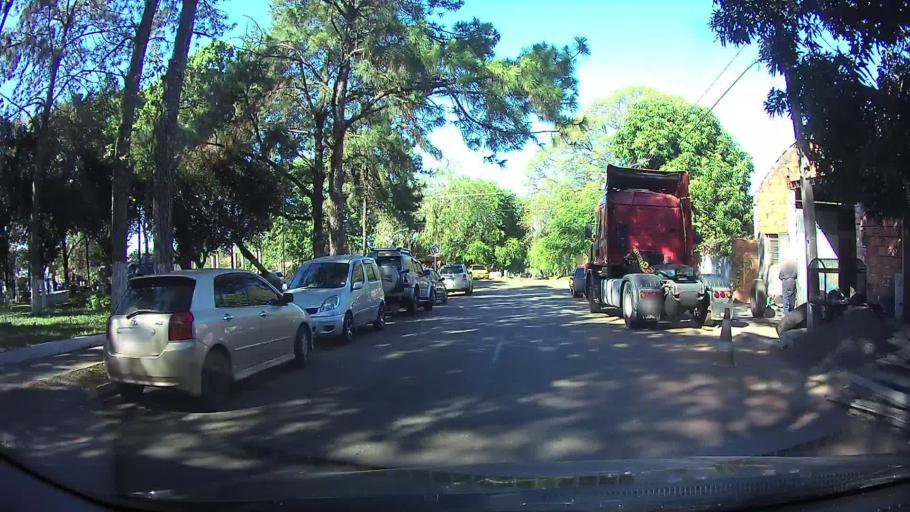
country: PY
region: Central
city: Villa Elisa
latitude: -25.3764
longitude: -57.5819
